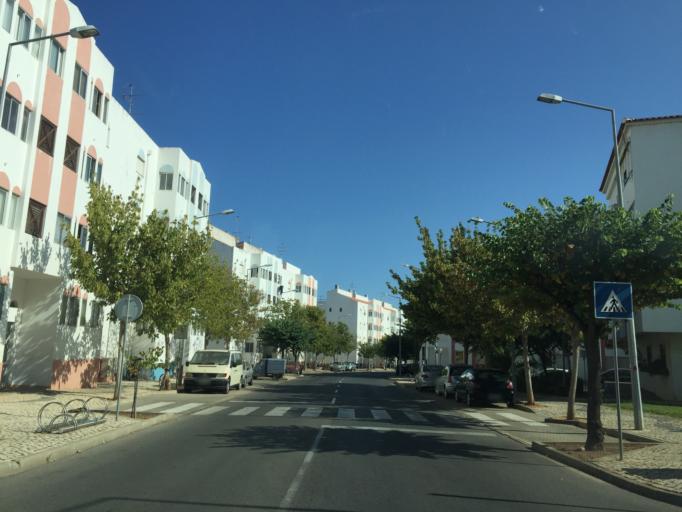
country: PT
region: Faro
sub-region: Tavira
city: Tavira
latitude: 37.1308
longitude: -7.6434
